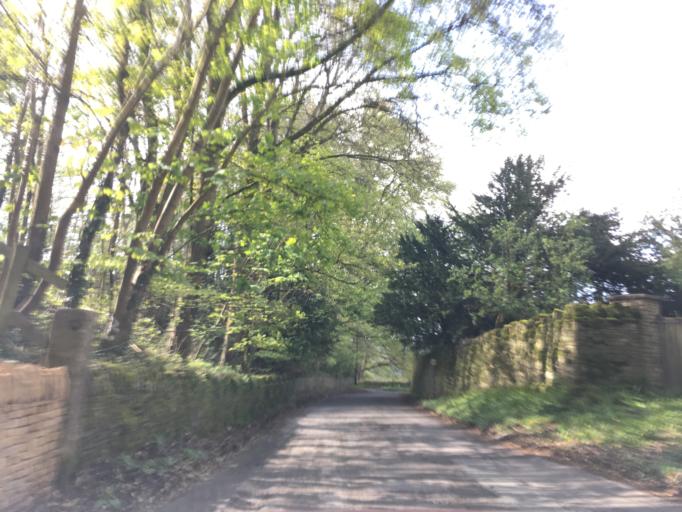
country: GB
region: England
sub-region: Gloucestershire
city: Minchinhampton
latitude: 51.7124
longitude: -2.1942
